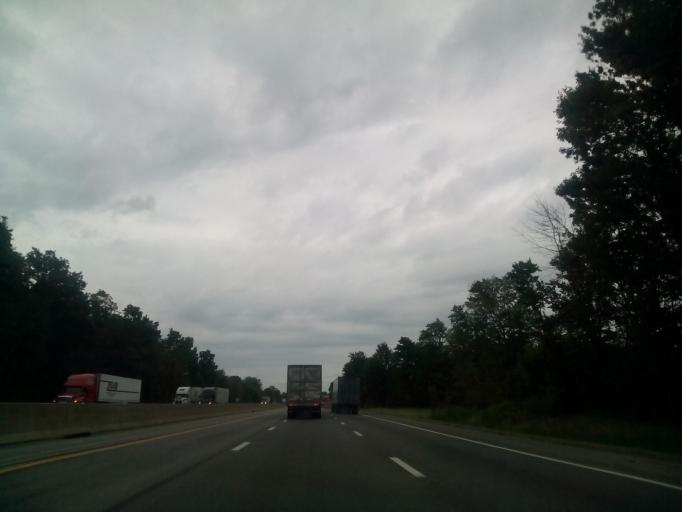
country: US
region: Ohio
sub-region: Huron County
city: Wakeman
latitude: 41.3315
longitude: -82.4414
